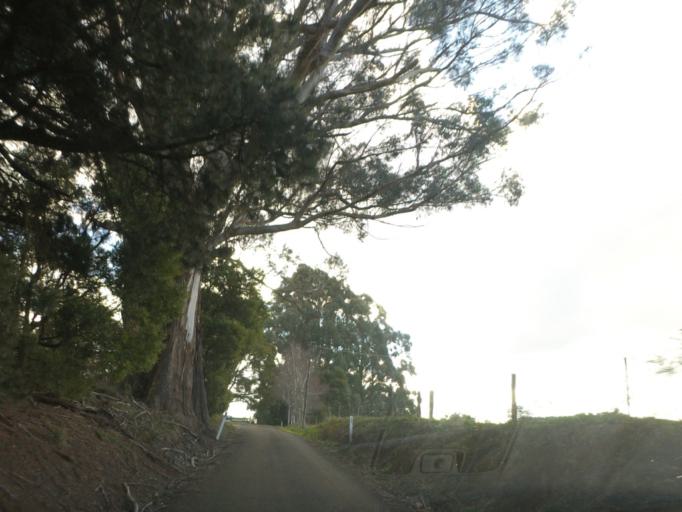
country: AU
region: Victoria
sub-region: Baw Baw
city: Warragul
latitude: -37.9277
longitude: 145.9476
